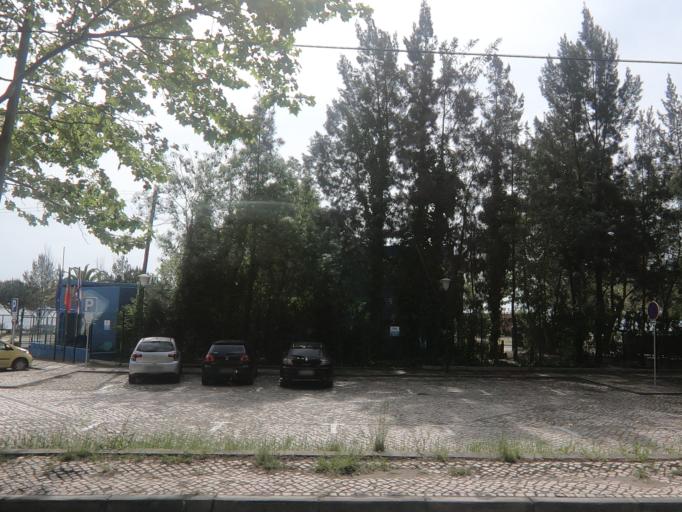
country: PT
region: Setubal
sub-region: Setubal
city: Setubal
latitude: 38.5030
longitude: -8.9290
